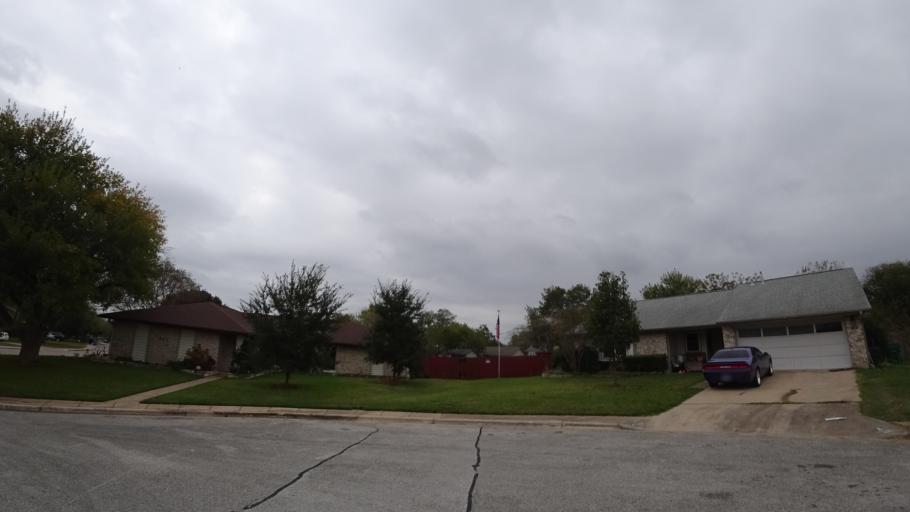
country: US
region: Texas
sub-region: Travis County
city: Pflugerville
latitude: 30.4296
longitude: -97.6099
